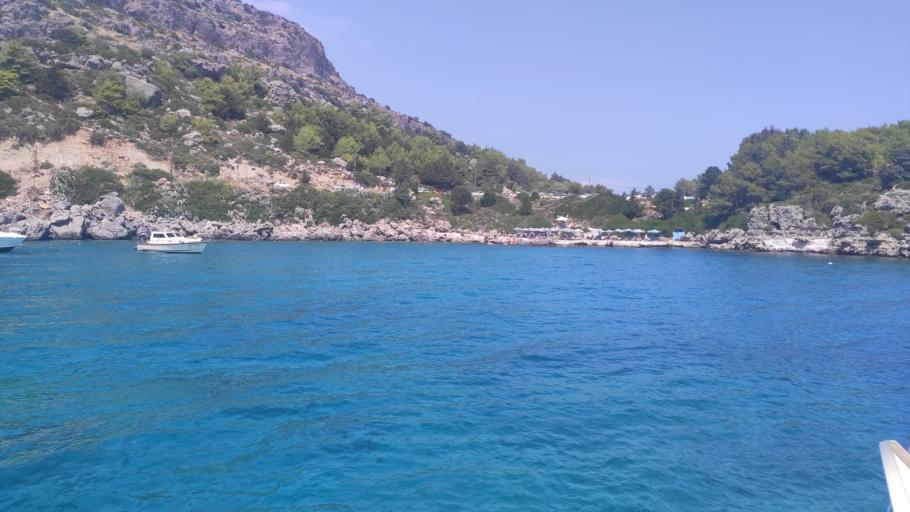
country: GR
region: South Aegean
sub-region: Nomos Dodekanisou
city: Faliraki
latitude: 36.3199
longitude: 28.2070
